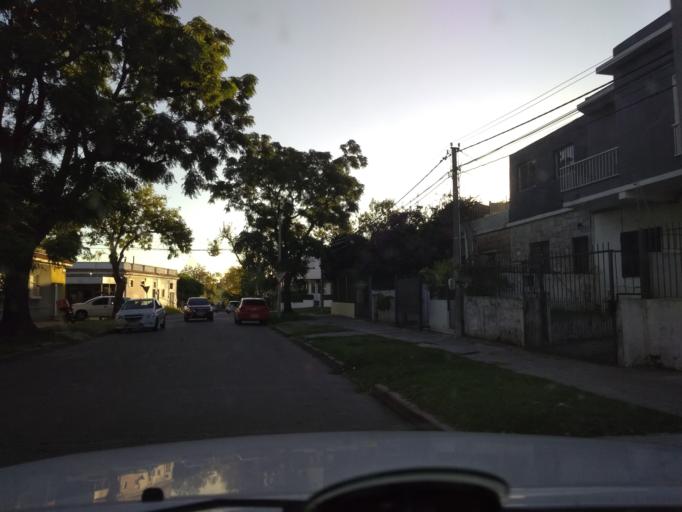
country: UY
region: Montevideo
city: Montevideo
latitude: -34.8911
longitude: -56.1397
